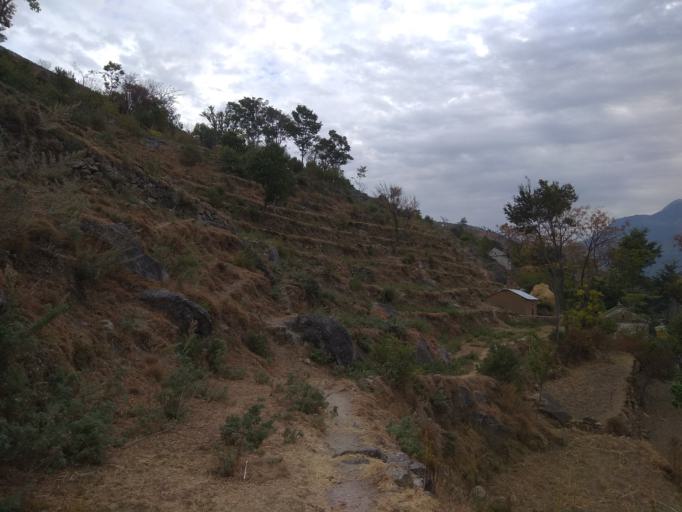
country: NP
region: Far Western
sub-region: Seti Zone
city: Achham
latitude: 29.2333
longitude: 81.6365
